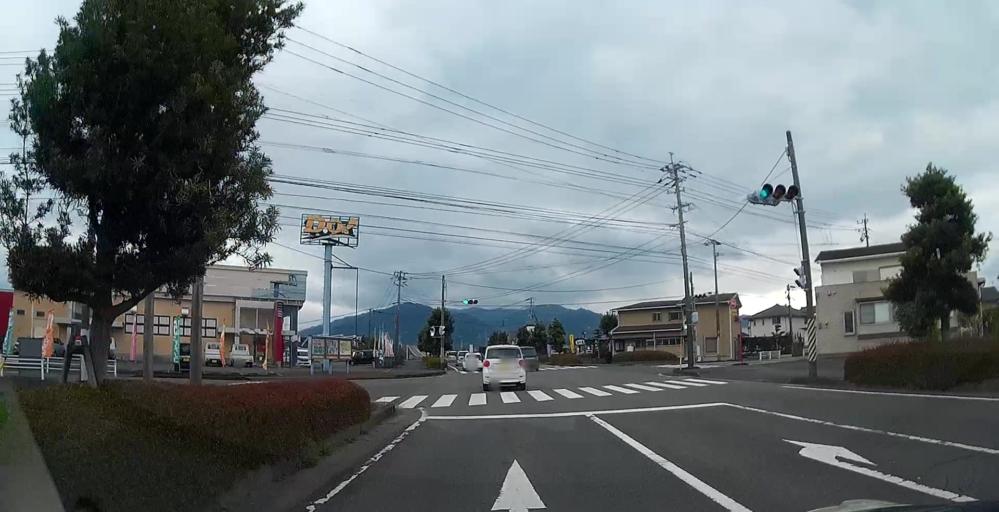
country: JP
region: Kagoshima
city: Izumi
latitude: 32.0812
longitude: 130.3445
